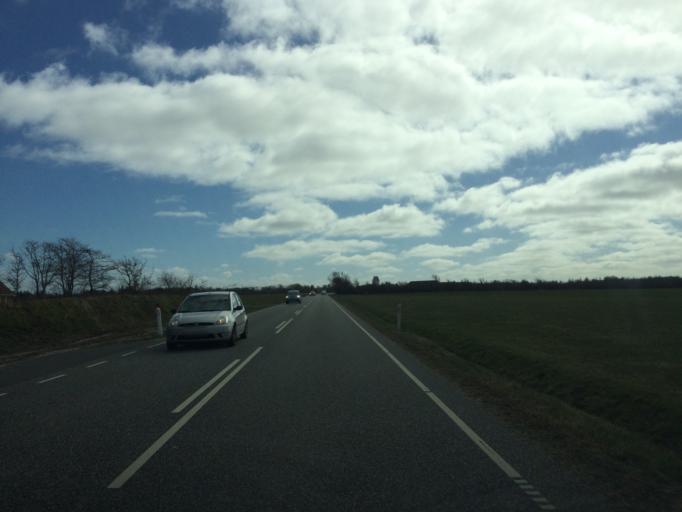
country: DK
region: Central Jutland
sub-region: Holstebro Kommune
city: Ulfborg
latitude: 56.3111
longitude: 8.1751
